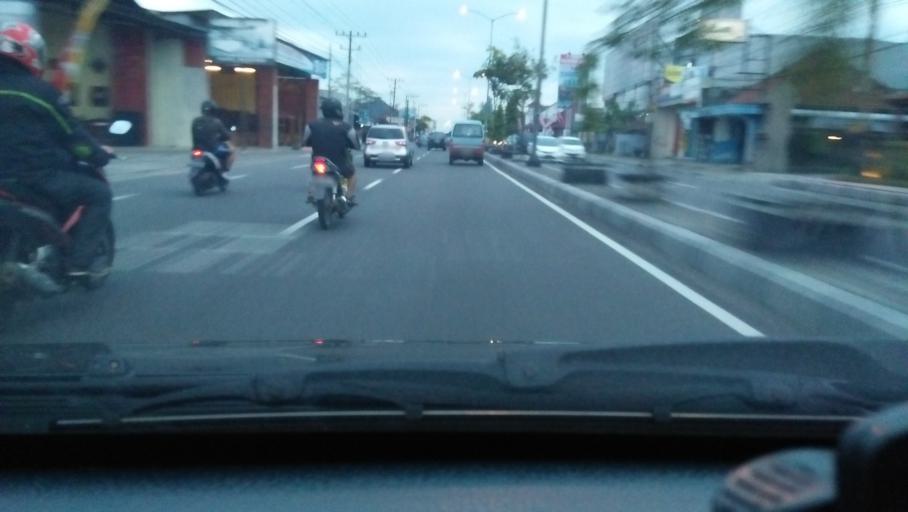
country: ID
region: Central Java
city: Mertoyudan
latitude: -7.5144
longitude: 110.2257
